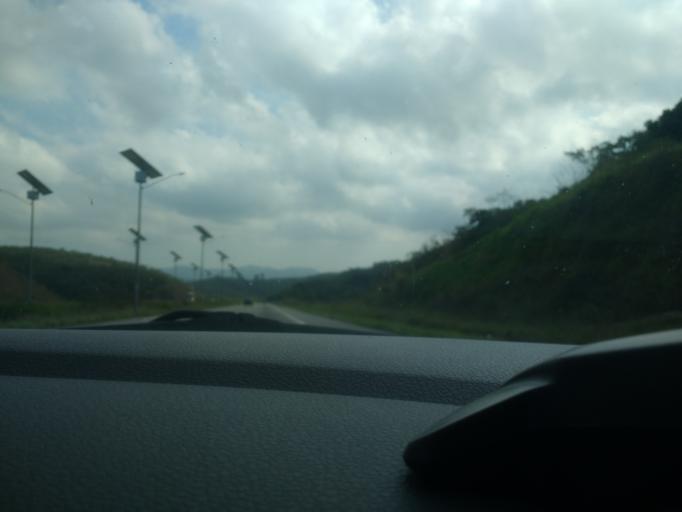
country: BR
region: Rio de Janeiro
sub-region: Queimados
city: Queimados
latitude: -22.6779
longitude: -43.5383
